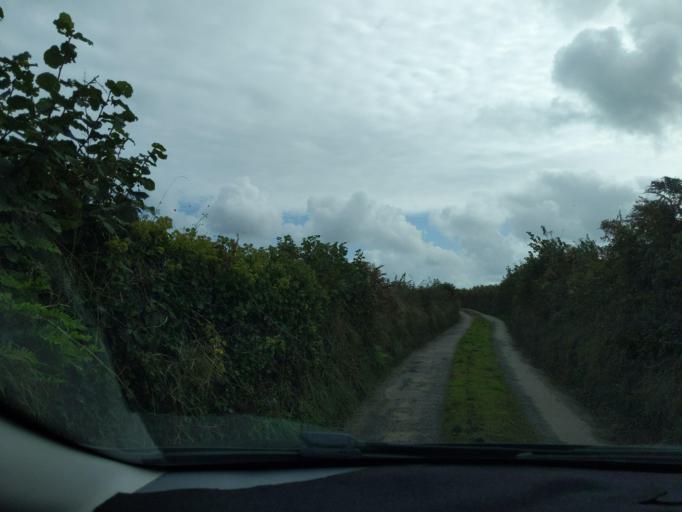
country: GB
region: England
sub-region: Cornwall
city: Par
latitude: 50.3890
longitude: -4.7029
